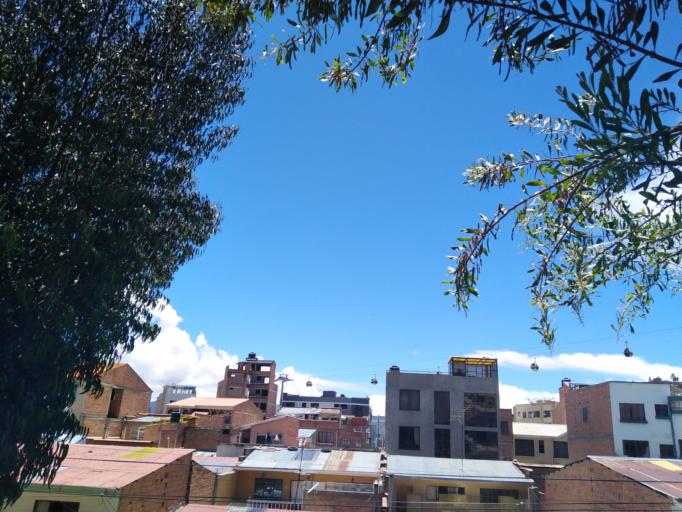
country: BO
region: La Paz
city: La Paz
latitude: -16.5136
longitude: -68.1401
